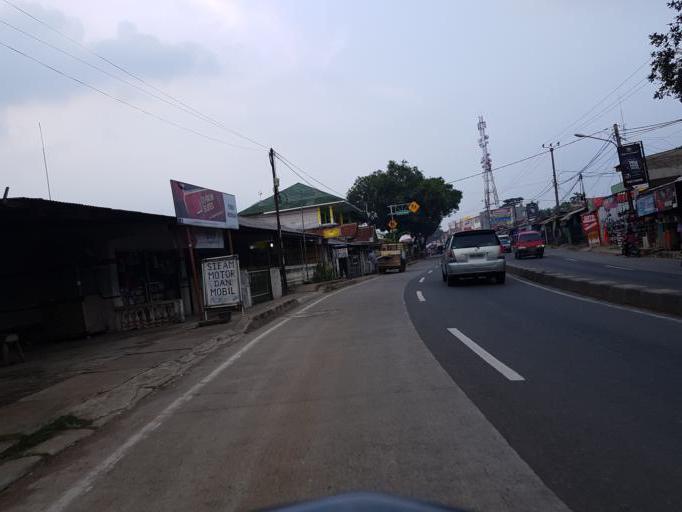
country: ID
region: West Java
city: Parung
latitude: -6.4817
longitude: 106.7314
